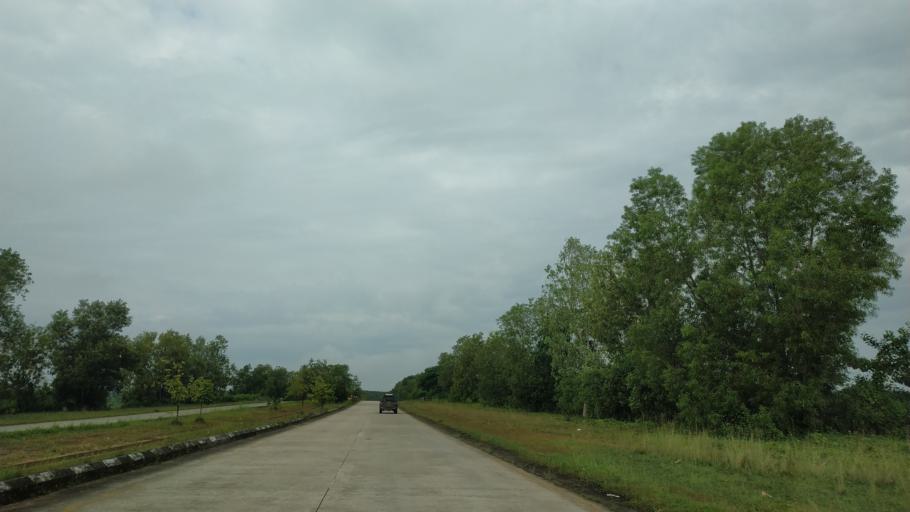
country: MM
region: Bago
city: Bago
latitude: 17.4622
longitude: 96.4329
